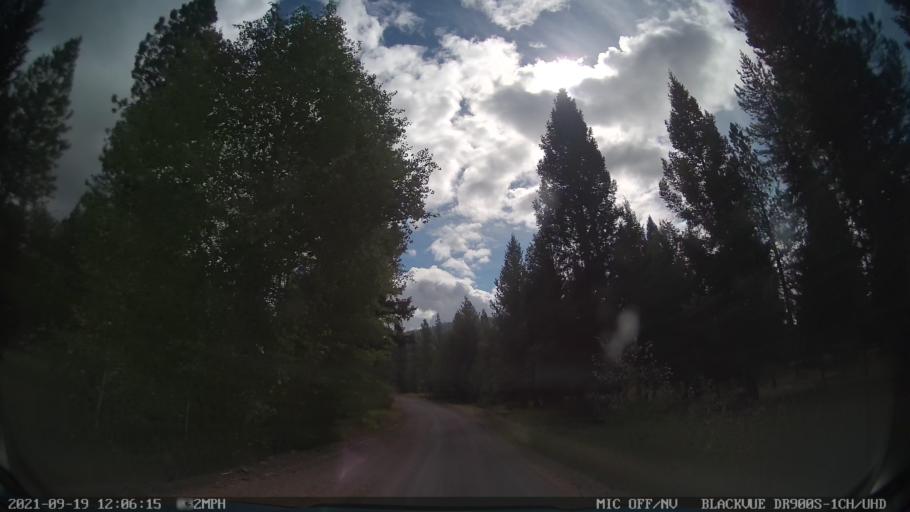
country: US
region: Montana
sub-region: Missoula County
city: Seeley Lake
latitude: 47.1859
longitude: -113.4210
